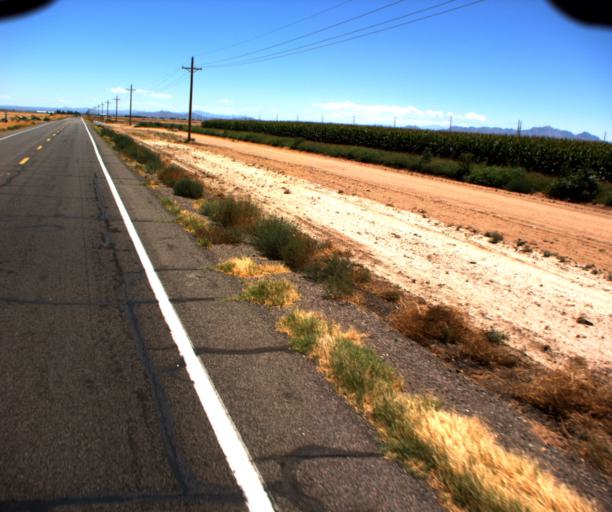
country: US
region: Arizona
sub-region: Pinal County
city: Coolidge
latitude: 32.8797
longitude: -111.6124
